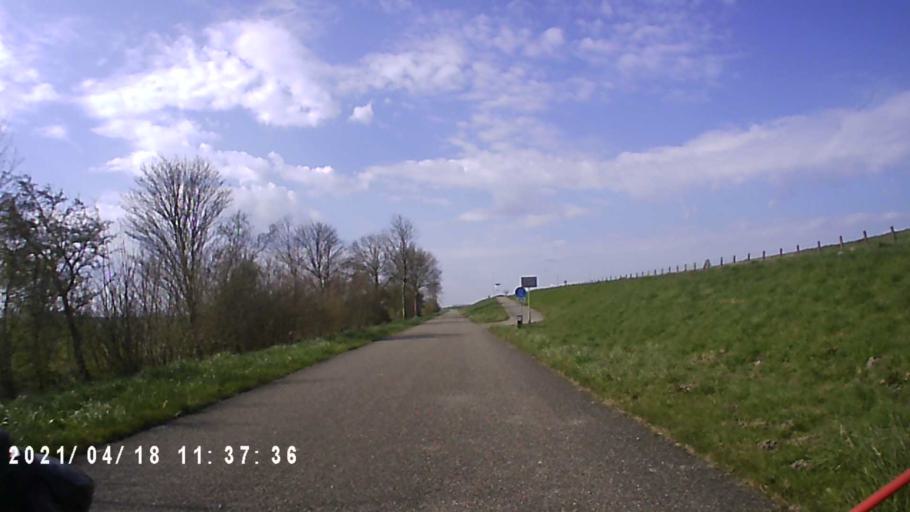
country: NL
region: Groningen
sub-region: Gemeente Zuidhorn
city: Grijpskerk
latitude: 53.3161
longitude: 6.2667
